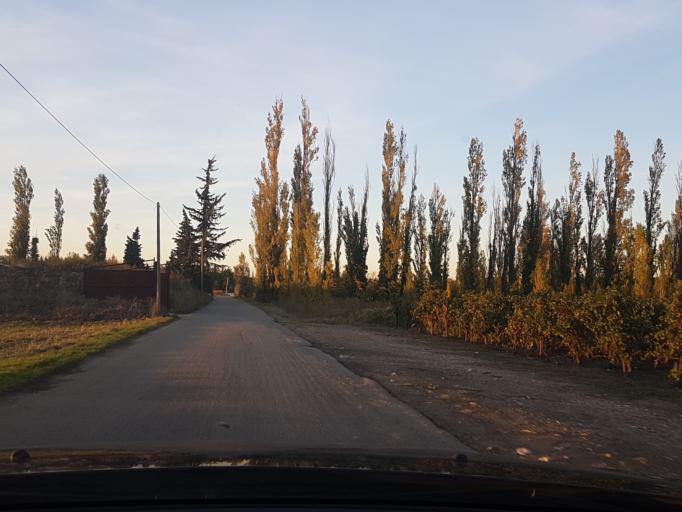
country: FR
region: Provence-Alpes-Cote d'Azur
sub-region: Departement du Vaucluse
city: Saint-Saturnin-les-Avignon
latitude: 43.9696
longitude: 4.9386
